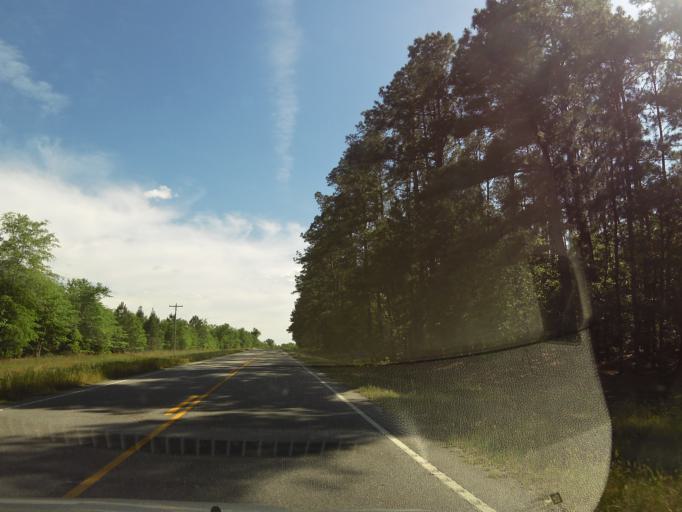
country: US
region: South Carolina
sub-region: Bamberg County
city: Denmark
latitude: 33.2599
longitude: -81.1580
